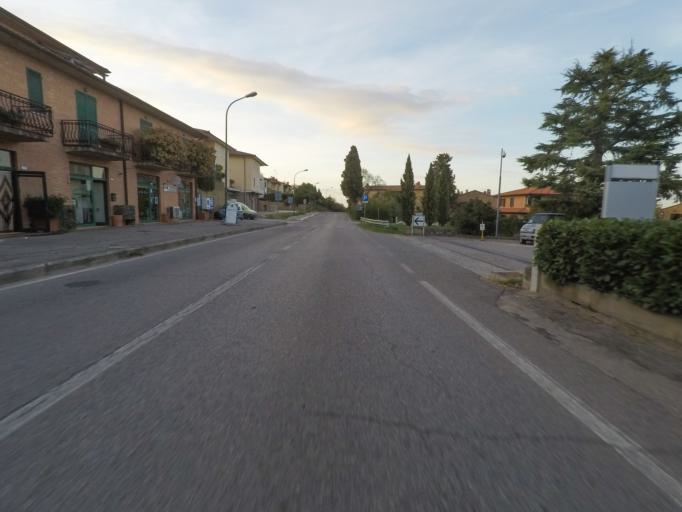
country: IT
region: Tuscany
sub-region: Provincia di Siena
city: Pienza
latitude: 43.0795
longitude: 11.6772
